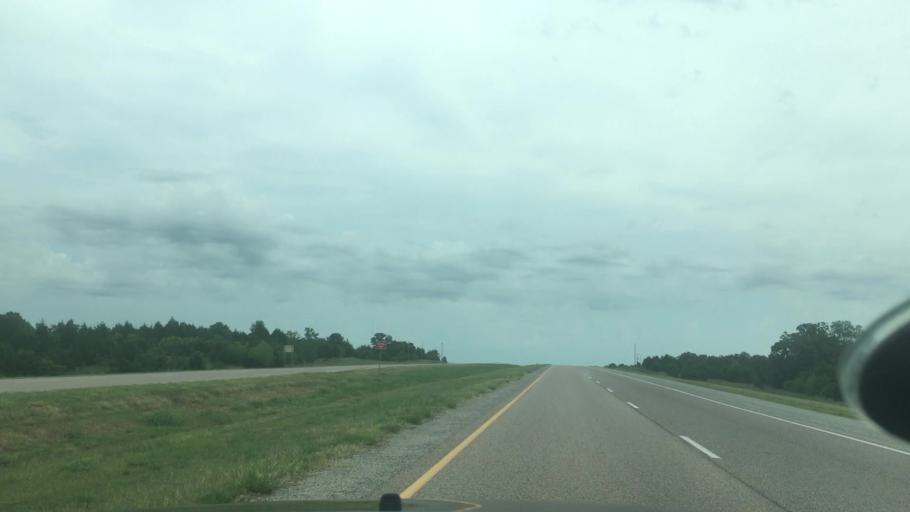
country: US
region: Oklahoma
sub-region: Pontotoc County
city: Byng
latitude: 34.8695
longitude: -96.6791
